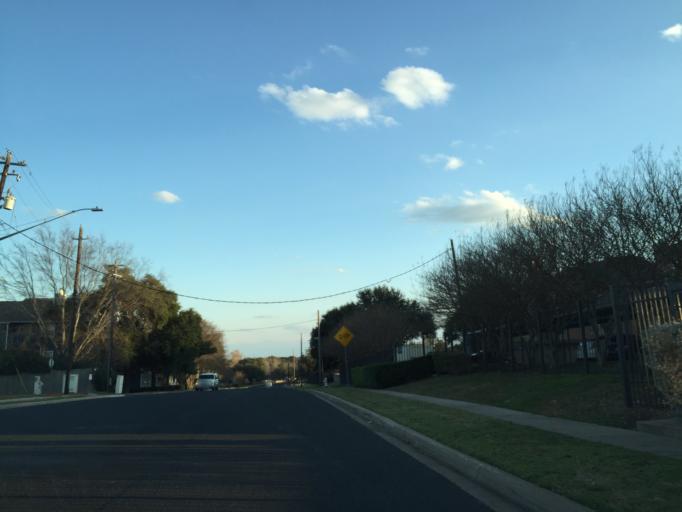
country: US
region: Texas
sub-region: Williamson County
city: Jollyville
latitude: 30.4416
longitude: -97.7459
